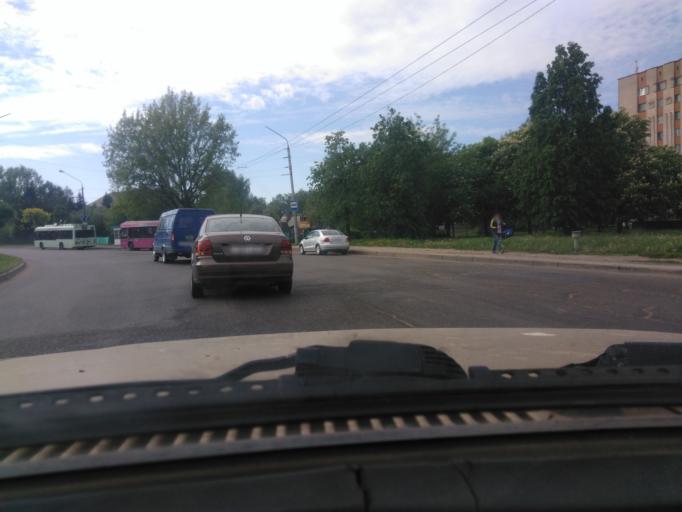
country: BY
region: Mogilev
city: Buynichy
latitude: 53.8983
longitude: 30.2937
